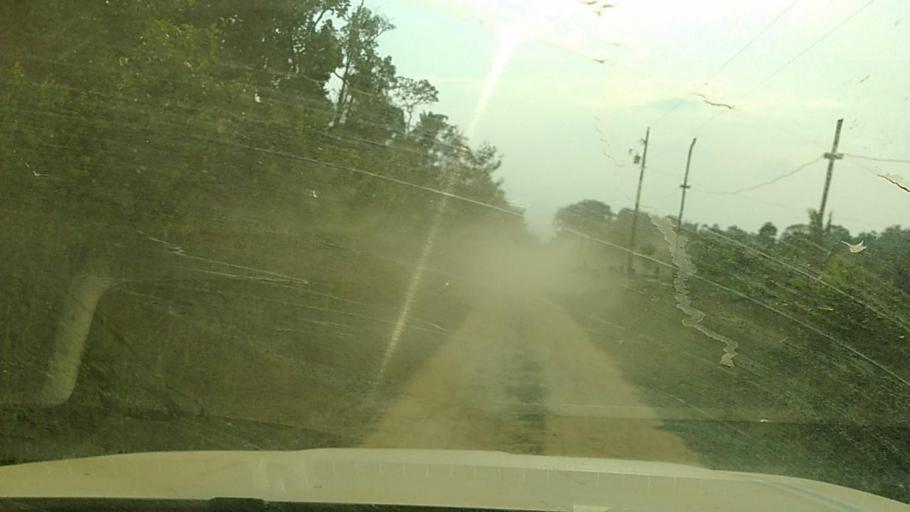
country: BR
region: Rondonia
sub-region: Porto Velho
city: Porto Velho
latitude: -8.5652
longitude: -64.0268
